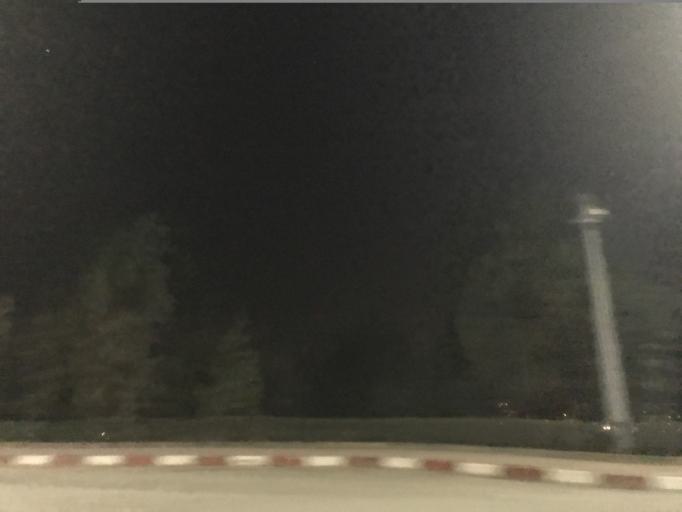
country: TR
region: Karabuk
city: Karabuk
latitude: 41.2126
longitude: 32.6529
